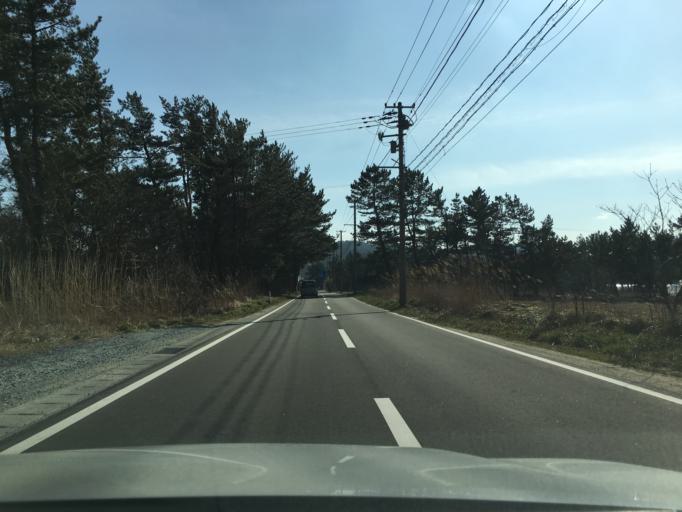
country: JP
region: Yamagata
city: Tsuruoka
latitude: 38.7952
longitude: 139.7695
